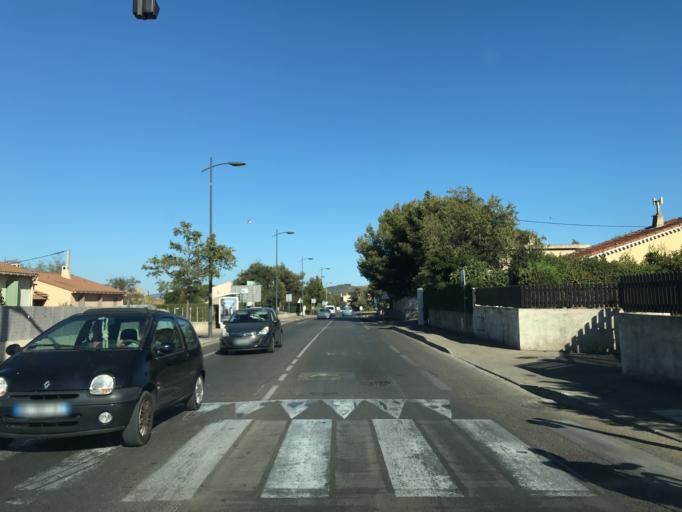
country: FR
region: Provence-Alpes-Cote d'Azur
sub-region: Departement du Var
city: La Seyne-sur-Mer
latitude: 43.0838
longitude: 5.8701
